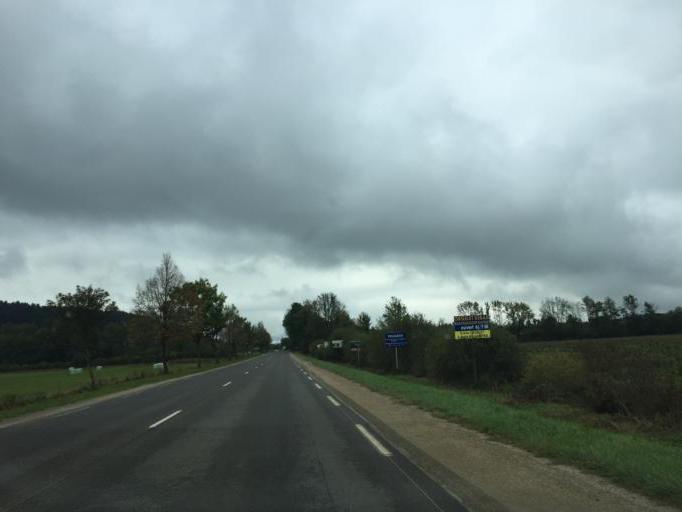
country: FR
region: Franche-Comte
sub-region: Departement du Jura
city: Orgelet
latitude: 46.5401
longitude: 5.6013
